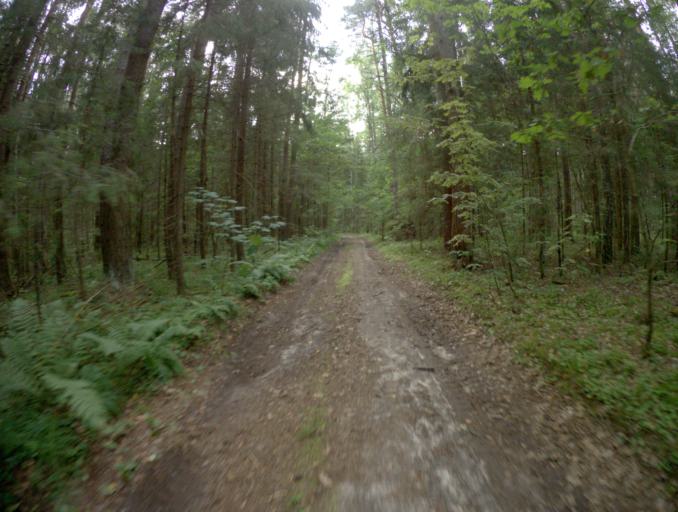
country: RU
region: Vladimir
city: Bogolyubovo
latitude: 56.1273
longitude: 40.5459
